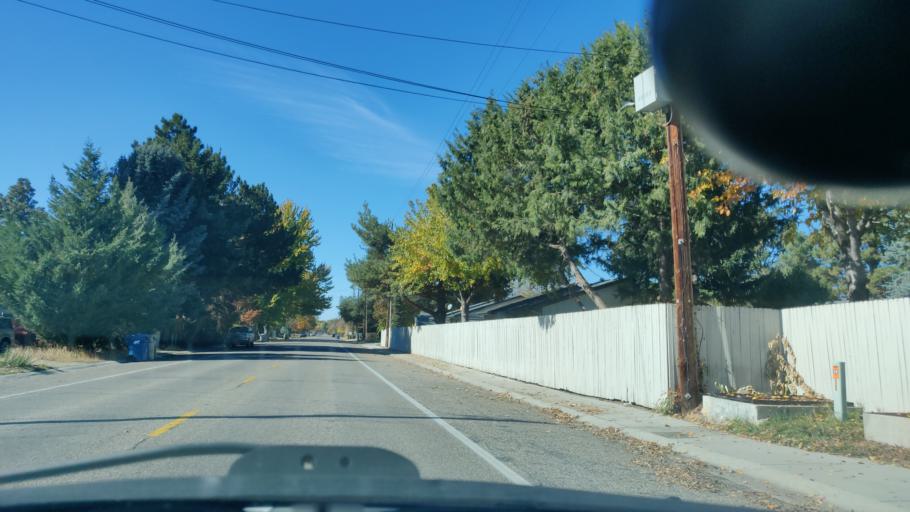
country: US
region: Idaho
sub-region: Ada County
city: Garden City
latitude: 43.5934
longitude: -116.2355
